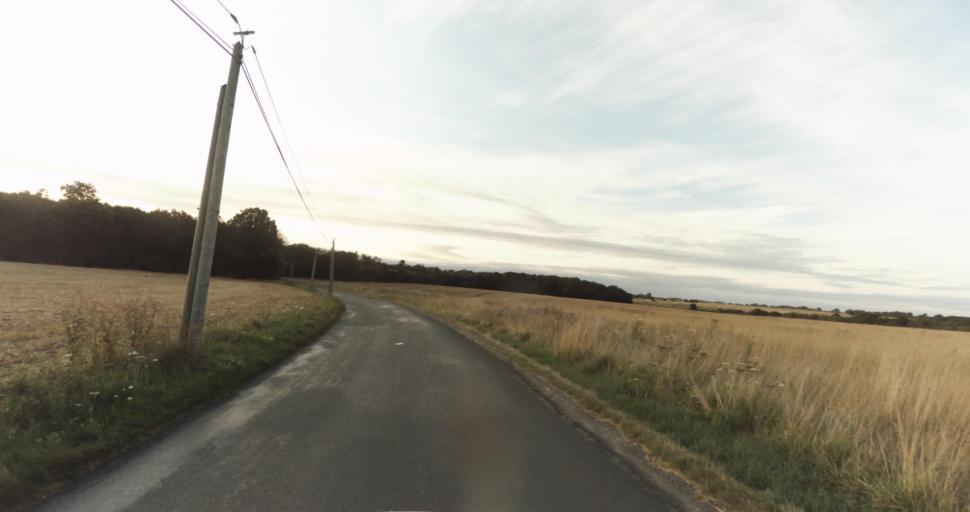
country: FR
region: Haute-Normandie
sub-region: Departement de l'Eure
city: Marcilly-sur-Eure
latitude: 48.8751
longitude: 1.2708
